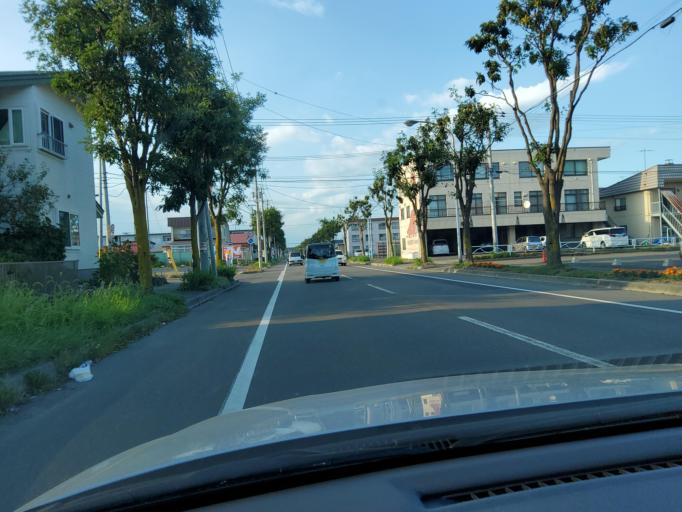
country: JP
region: Hokkaido
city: Obihiro
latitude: 42.9329
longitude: 143.1847
